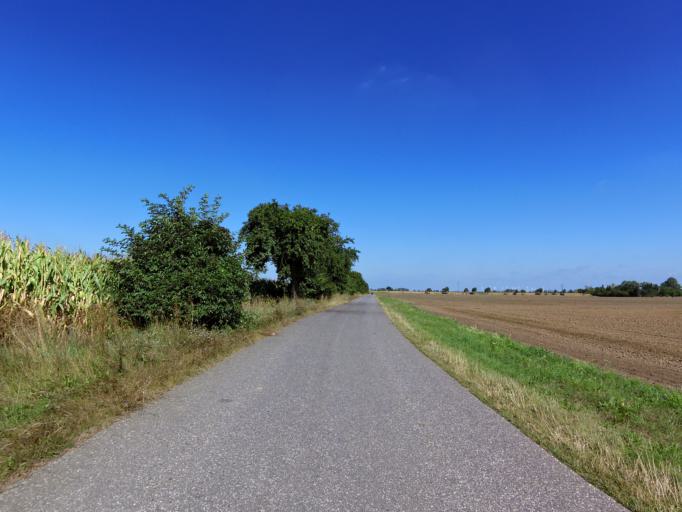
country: DE
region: Brandenburg
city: Muhlberg
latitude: 51.4000
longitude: 13.2438
